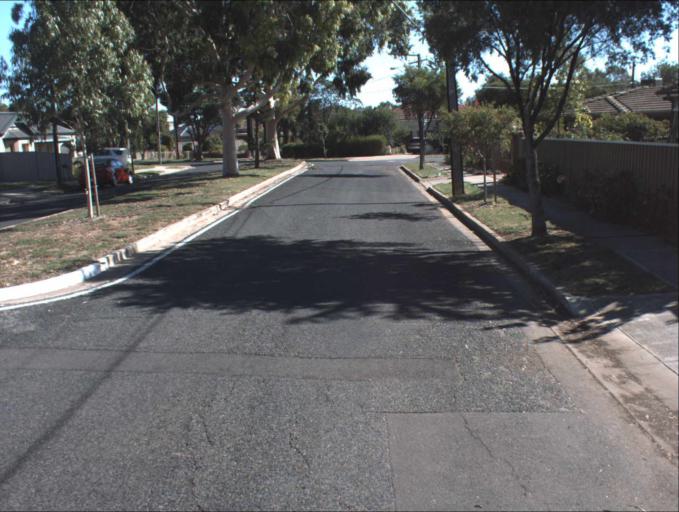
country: AU
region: South Australia
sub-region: Prospect
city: Prospect
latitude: -34.8738
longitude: 138.6131
